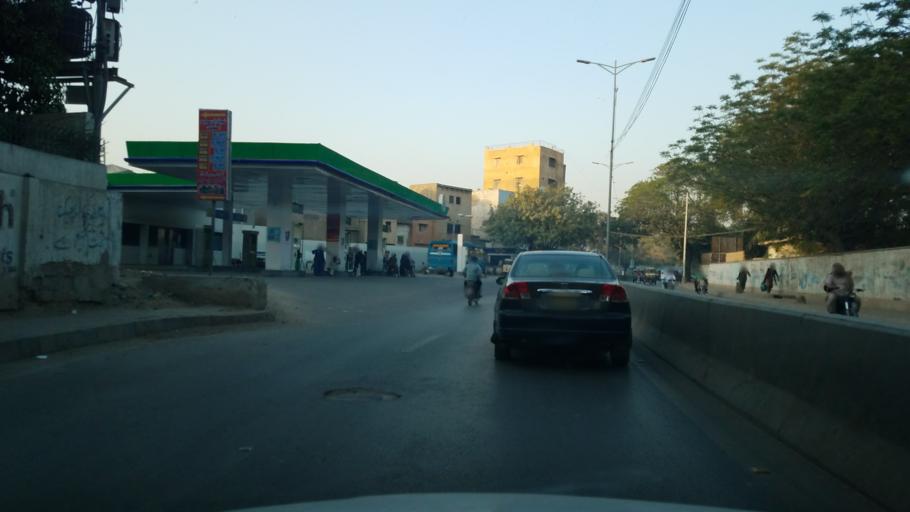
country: PK
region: Sindh
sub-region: Karachi District
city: Karachi
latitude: 24.8722
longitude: 67.0221
